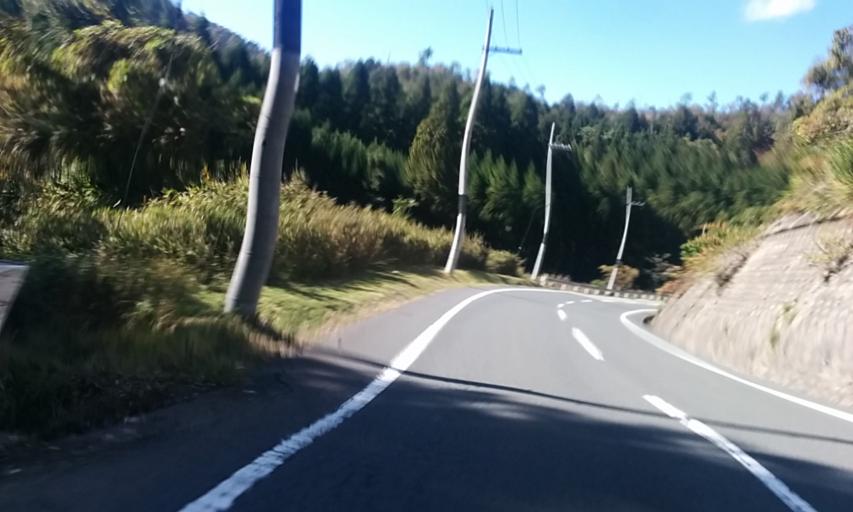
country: JP
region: Kyoto
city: Kameoka
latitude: 35.1216
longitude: 135.5619
